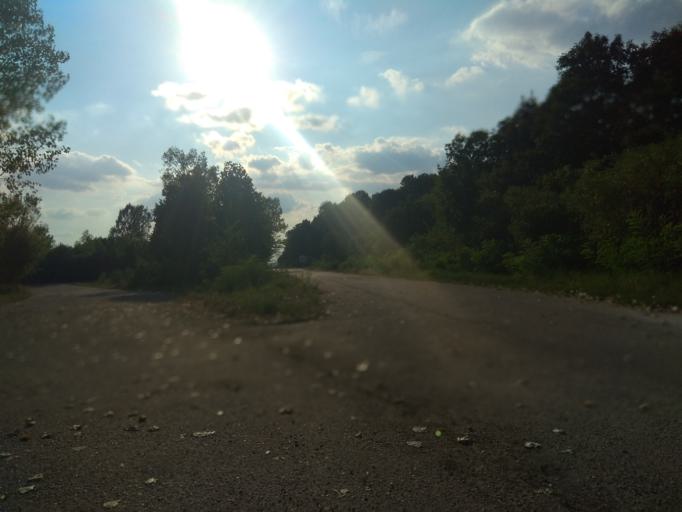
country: HU
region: Borsod-Abauj-Zemplen
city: Harsany
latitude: 47.9215
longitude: 20.7233
